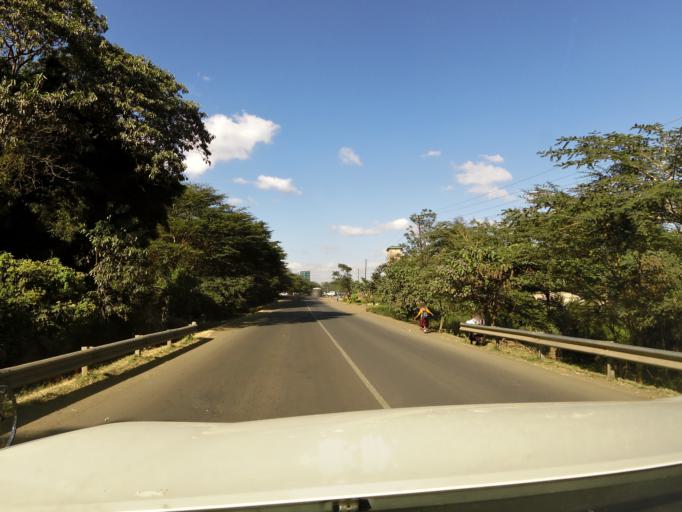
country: TZ
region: Arusha
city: Arusha
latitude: -3.3765
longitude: 36.6530
